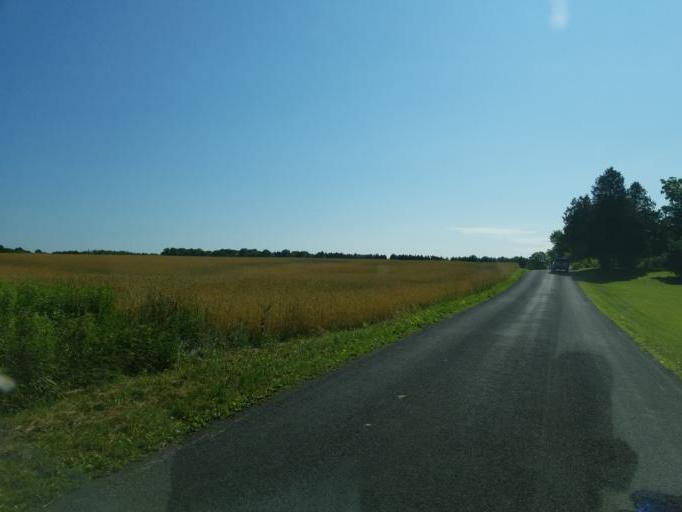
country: US
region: New York
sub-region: Wayne County
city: Clyde
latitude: 43.0546
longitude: -76.8943
